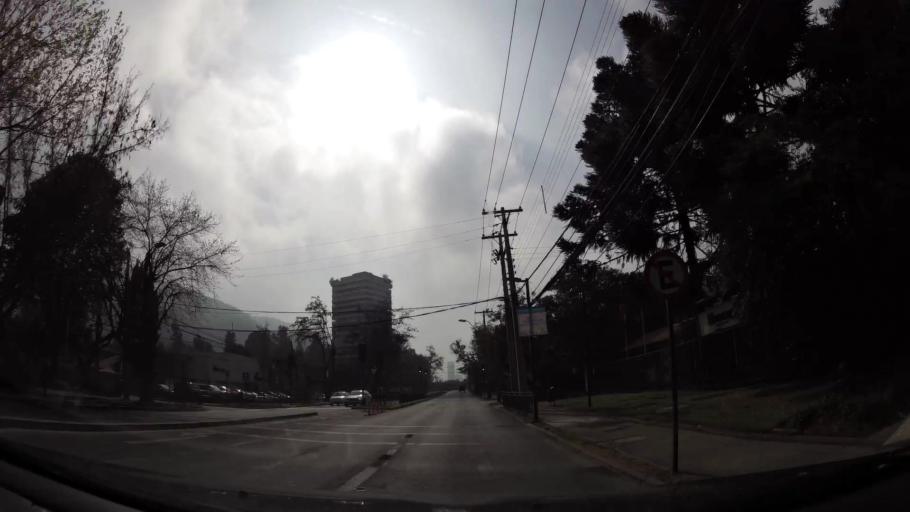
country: CL
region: Santiago Metropolitan
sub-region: Provincia de Santiago
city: Villa Presidente Frei, Nunoa, Santiago, Chile
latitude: -33.3801
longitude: -70.5413
